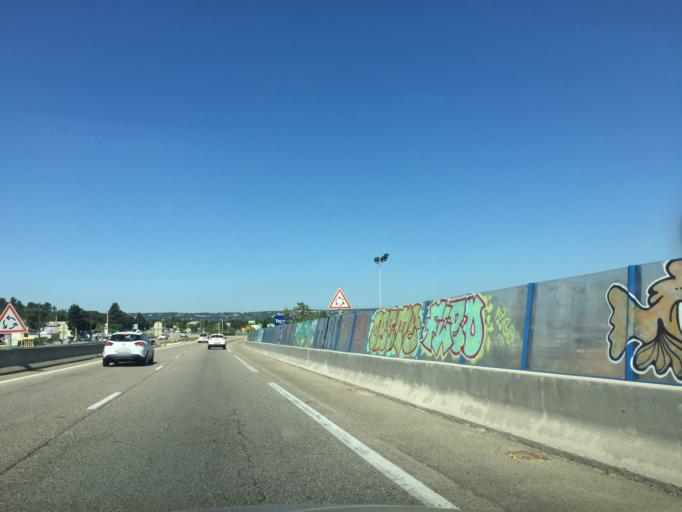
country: FR
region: Languedoc-Roussillon
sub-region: Departement du Gard
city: Les Angles
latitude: 43.9584
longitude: 4.7370
